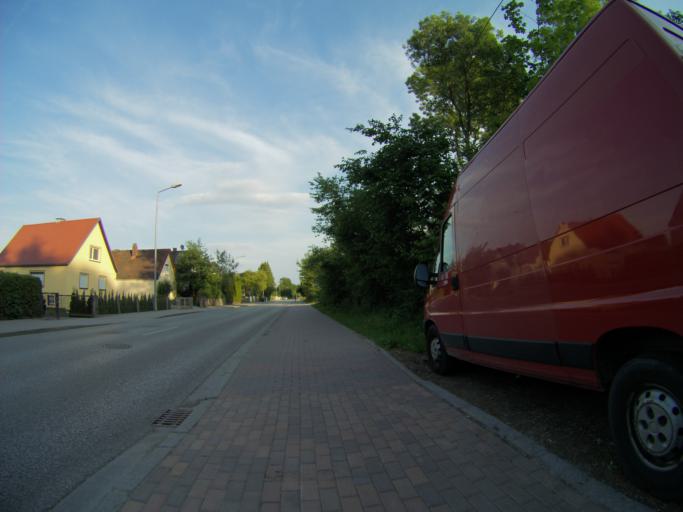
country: DE
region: Bavaria
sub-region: Upper Bavaria
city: Freising
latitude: 48.3881
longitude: 11.7655
